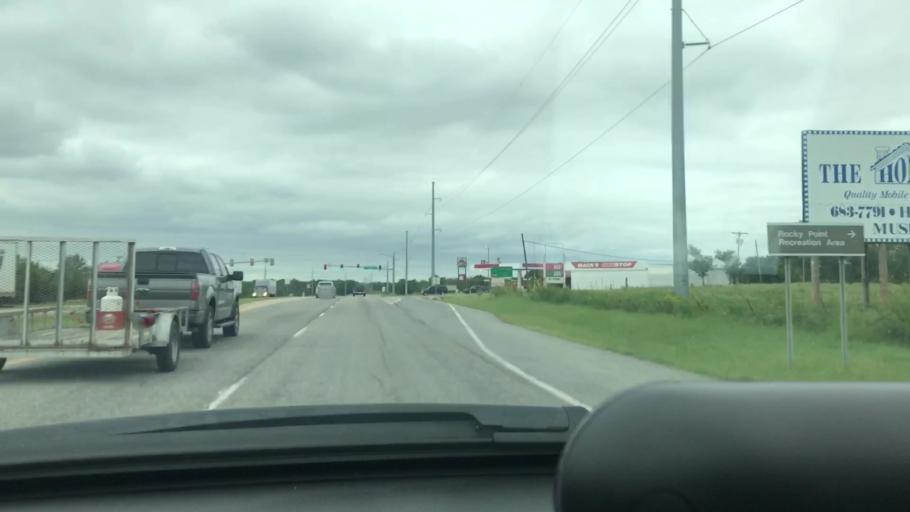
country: US
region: Oklahoma
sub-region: Wagoner County
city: Wagoner
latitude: 36.0160
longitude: -95.3680
